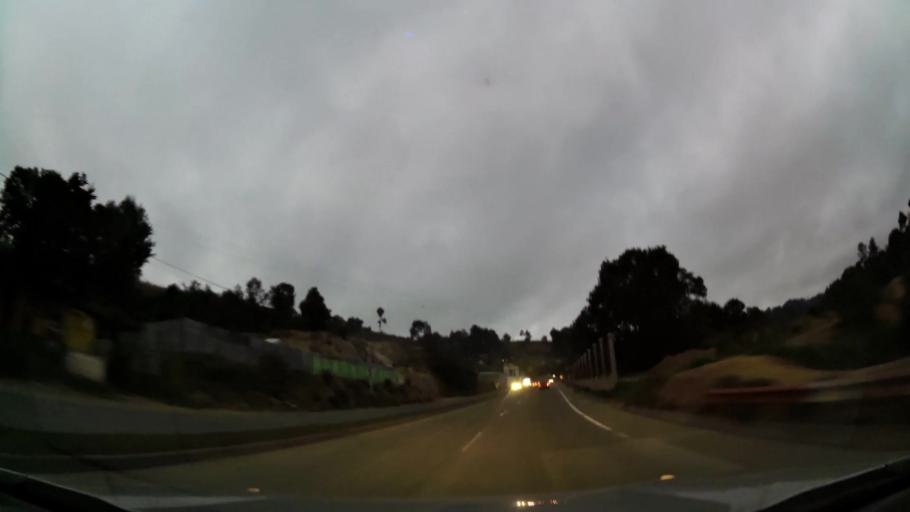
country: GT
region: Chimaltenango
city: Santa Apolonia
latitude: 14.8244
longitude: -91.0249
